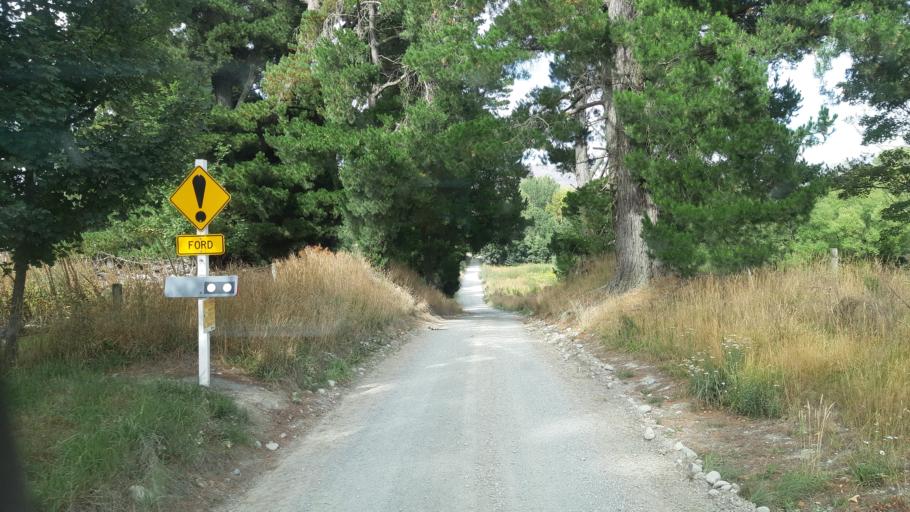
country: NZ
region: Canterbury
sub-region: Timaru District
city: Pleasant Point
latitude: -44.0347
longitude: 170.7580
